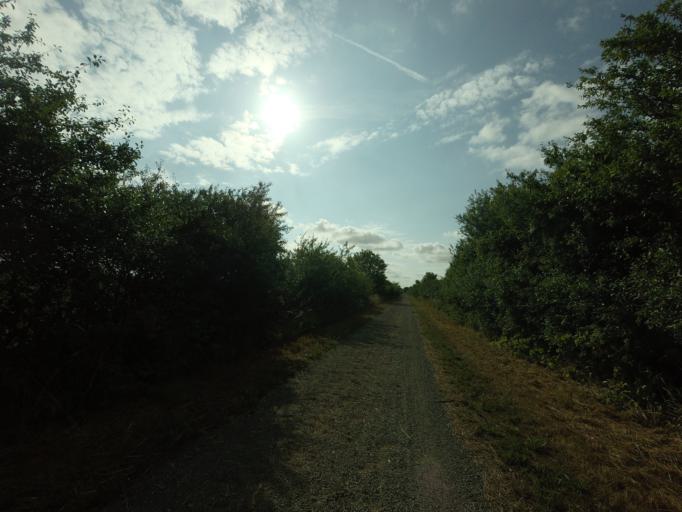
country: SE
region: Skane
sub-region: Helsingborg
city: Odakra
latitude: 56.1588
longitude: 12.7488
